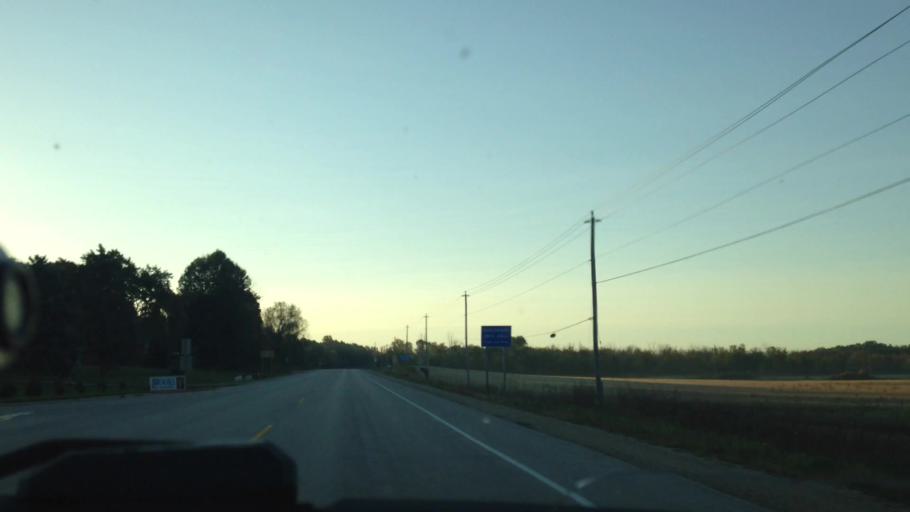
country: US
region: Wisconsin
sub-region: Washington County
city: Newburg
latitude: 43.4280
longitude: -88.0394
